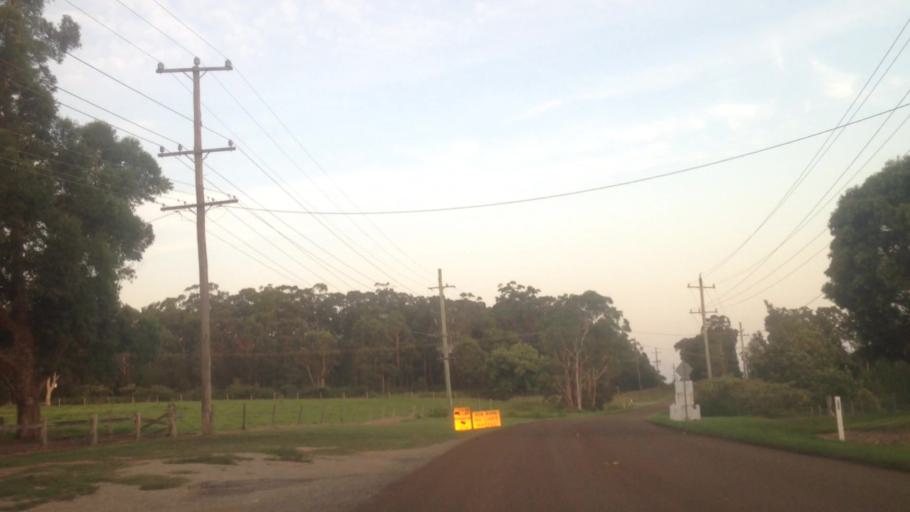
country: AU
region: New South Wales
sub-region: Lake Macquarie Shire
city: Dora Creek
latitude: -33.0741
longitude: 151.4831
